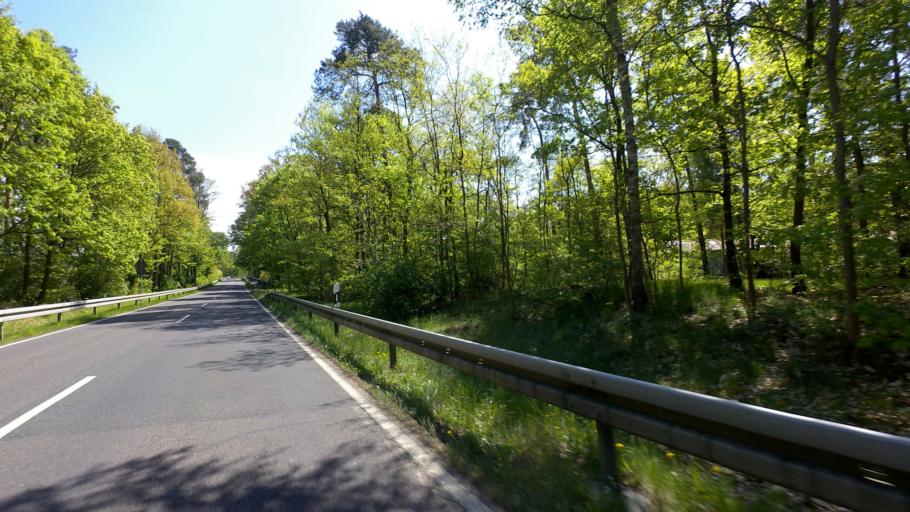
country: DE
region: Brandenburg
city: Gross Koris
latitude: 52.1864
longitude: 13.7006
